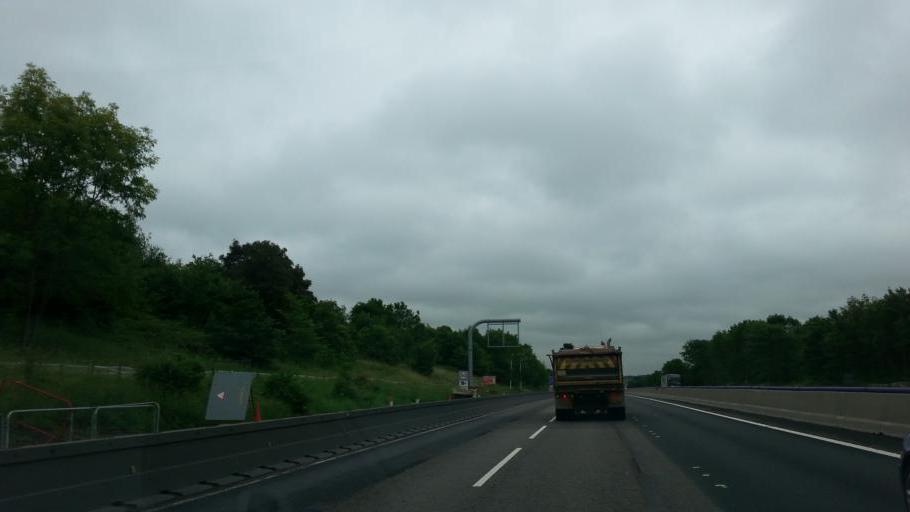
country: GB
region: England
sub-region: Leicestershire
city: Lutterworth
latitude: 52.3666
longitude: -1.1596
